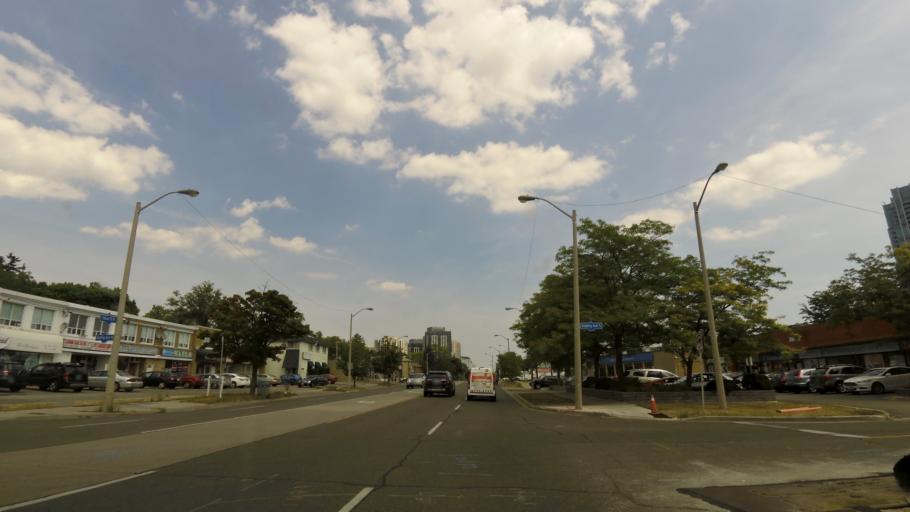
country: CA
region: Ontario
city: Etobicoke
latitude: 43.6408
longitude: -79.5397
